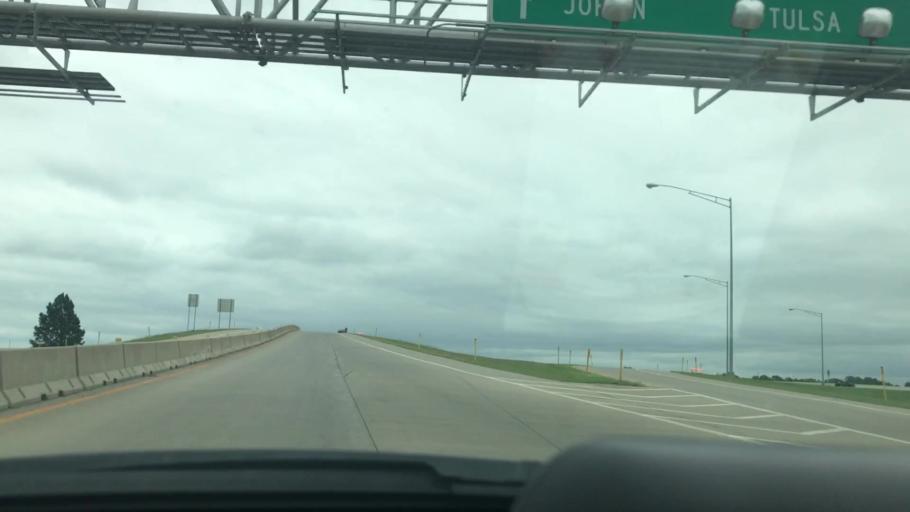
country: US
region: Oklahoma
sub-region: Craig County
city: Vinita
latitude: 36.5668
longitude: -95.2168
